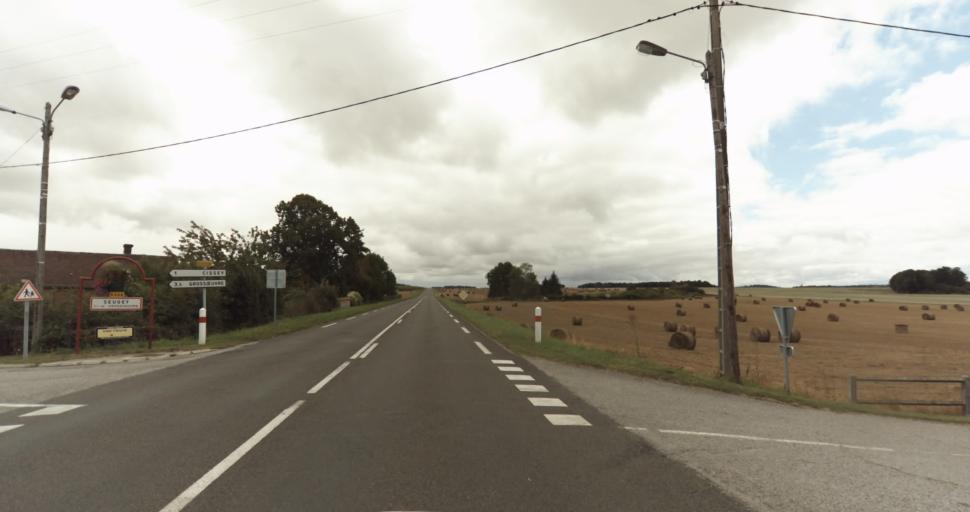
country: FR
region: Haute-Normandie
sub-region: Departement de l'Eure
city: Evreux
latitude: 48.9538
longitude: 1.1622
